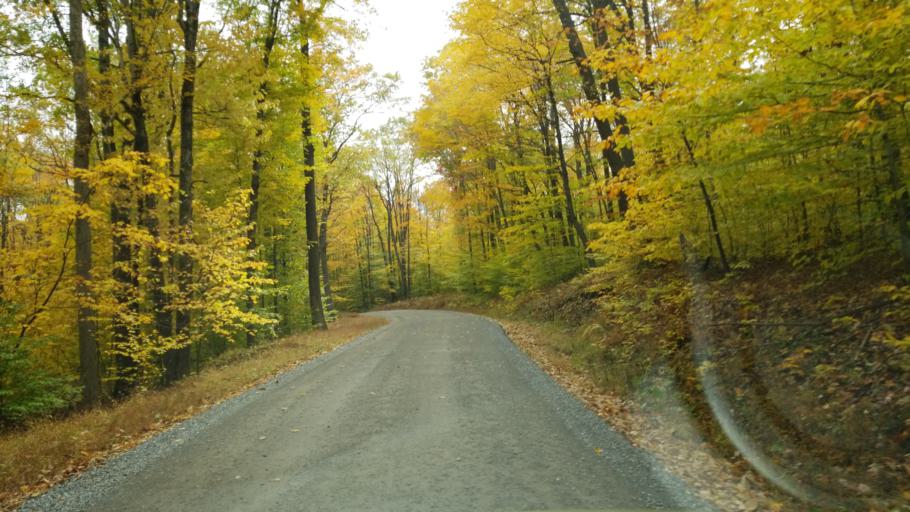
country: US
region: Pennsylvania
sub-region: Clearfield County
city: Clearfield
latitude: 41.1938
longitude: -78.3854
